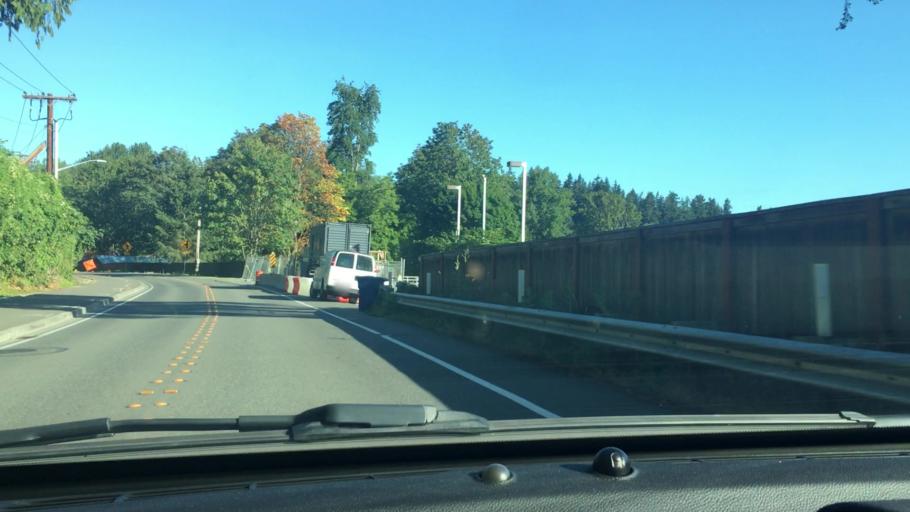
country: US
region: Washington
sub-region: King County
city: West Lake Sammamish
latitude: 47.5758
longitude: -122.1109
